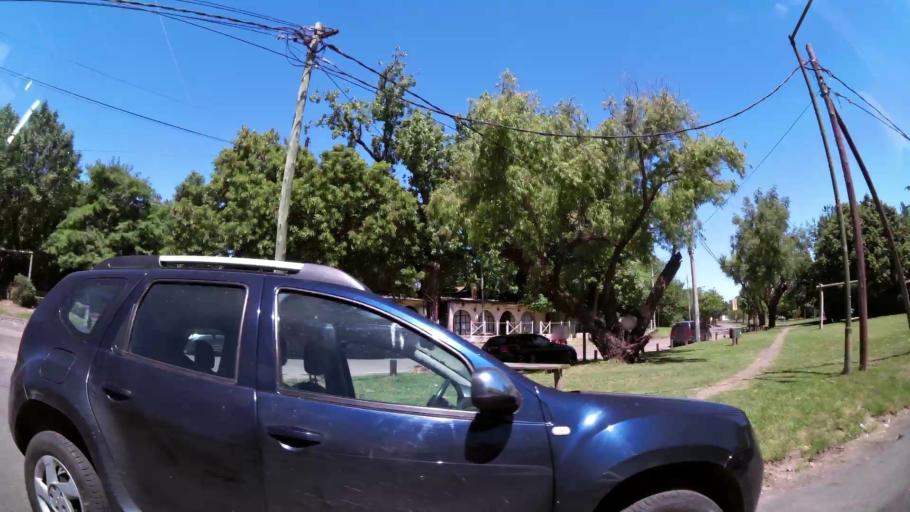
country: AR
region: Buenos Aires
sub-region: Partido de San Isidro
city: San Isidro
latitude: -34.4596
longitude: -58.5067
